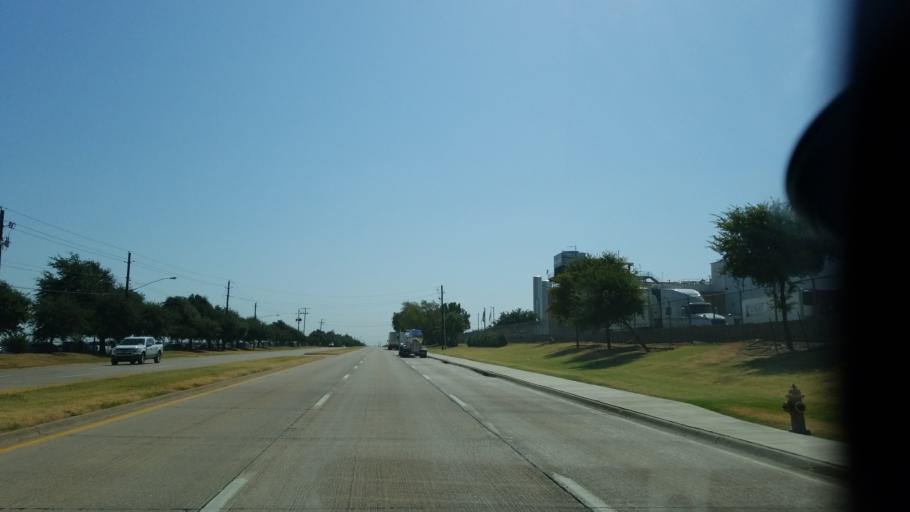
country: US
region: Texas
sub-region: Dallas County
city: Cockrell Hill
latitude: 32.7057
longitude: -96.9213
